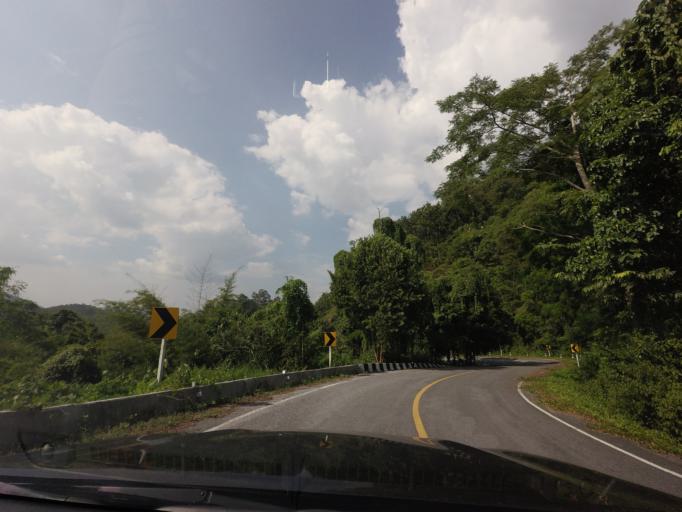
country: TH
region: Uttaradit
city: Ban Khok
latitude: 18.2535
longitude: 100.9947
